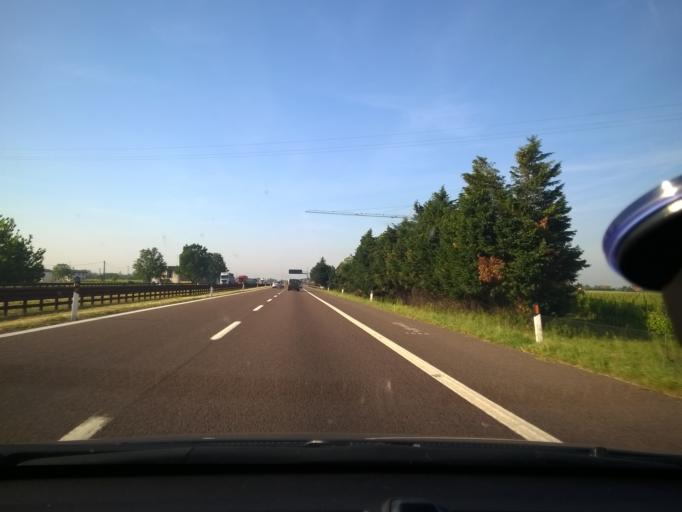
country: IT
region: Emilia-Romagna
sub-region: Provincia di Modena
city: Santa Croce Scuole
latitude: 44.7335
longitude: 10.8440
